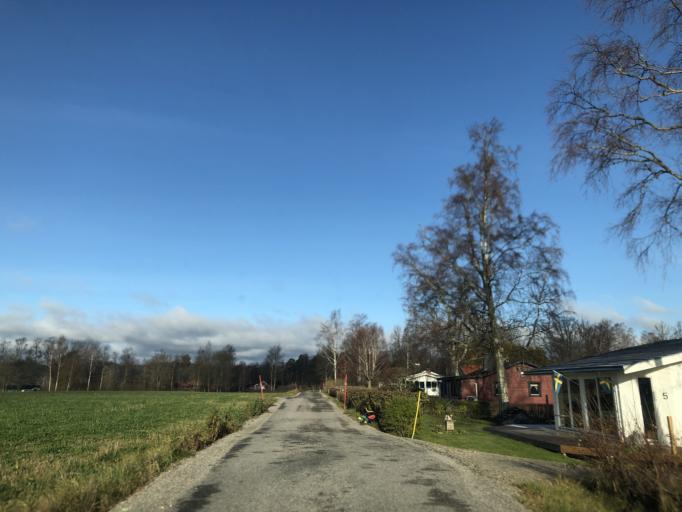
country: SE
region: Vaestra Goetaland
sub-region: Ulricehamns Kommun
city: Ulricehamn
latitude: 57.7219
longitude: 13.3984
